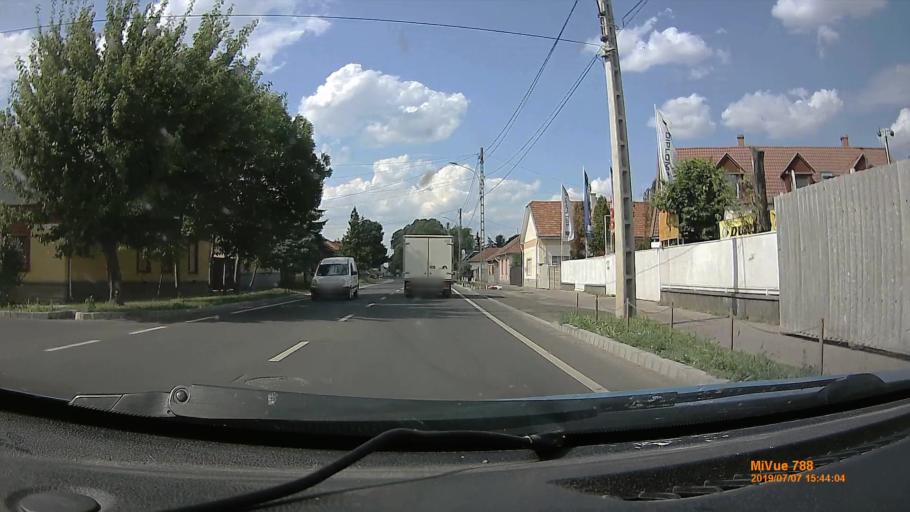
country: HU
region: Jasz-Nagykun-Szolnok
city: Jaszbereny
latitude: 47.5065
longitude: 19.9100
